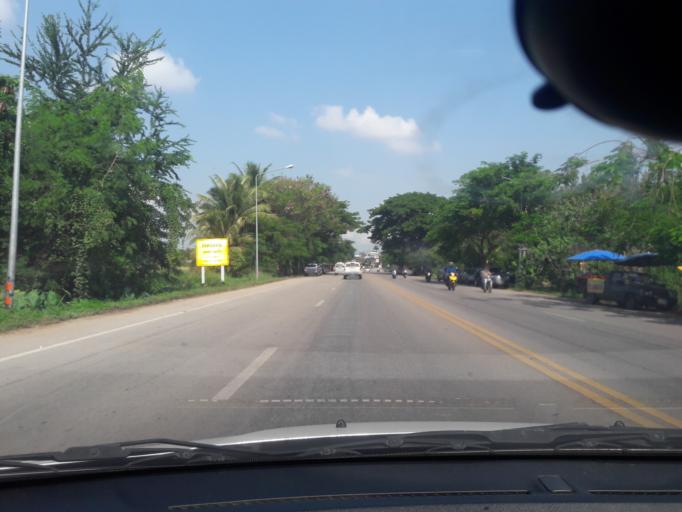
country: TH
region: Lampang
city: Lampang
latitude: 18.2450
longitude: 99.4911
